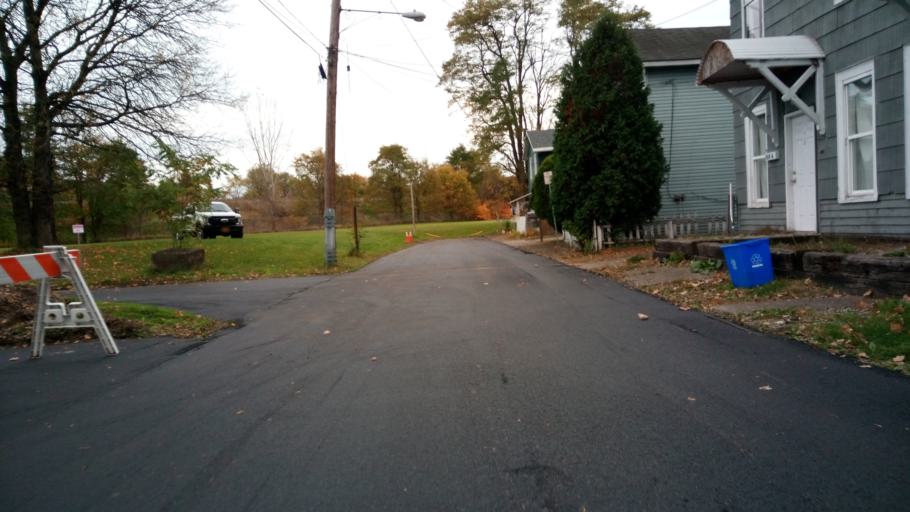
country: US
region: New York
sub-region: Chemung County
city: Elmira
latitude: 42.0731
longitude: -76.8025
